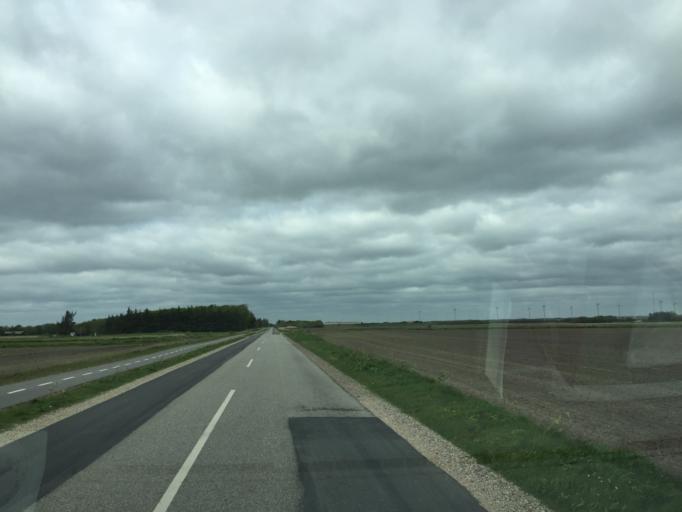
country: DK
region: Central Jutland
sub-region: Ringkobing-Skjern Kommune
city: Ringkobing
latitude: 56.0193
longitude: 8.3116
